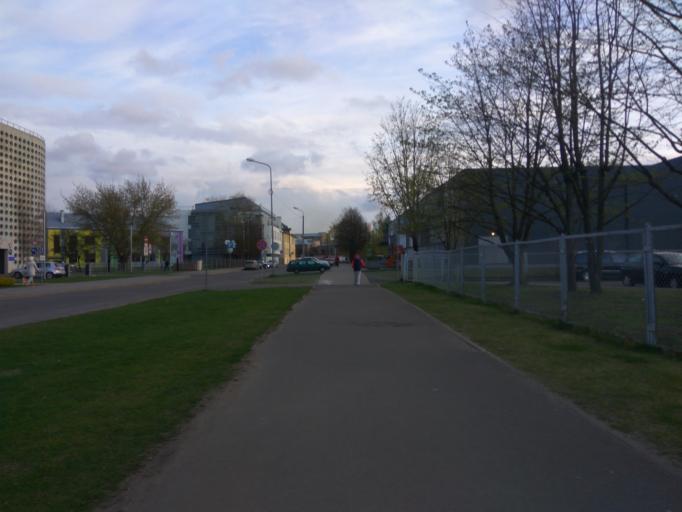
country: LV
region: Riga
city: Riga
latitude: 56.9651
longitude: 24.1207
